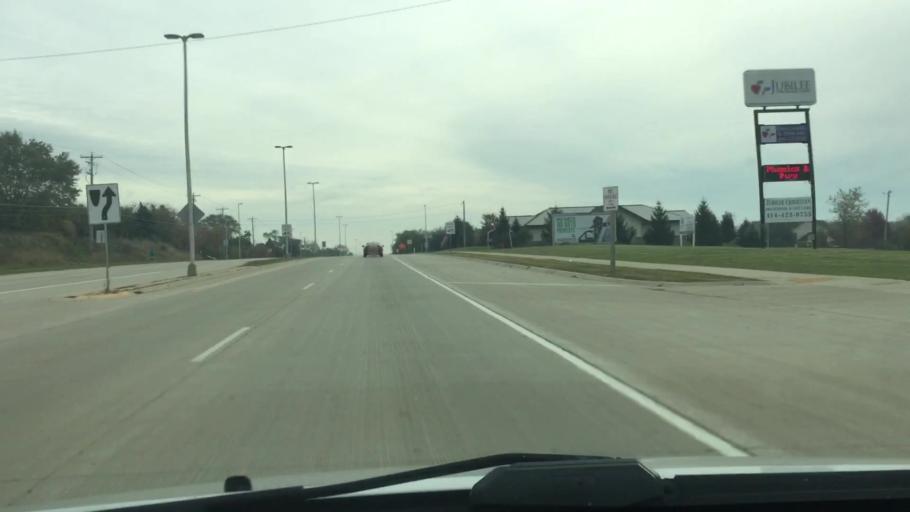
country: US
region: Wisconsin
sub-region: Milwaukee County
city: Greendale
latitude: 42.8726
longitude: -87.9637
